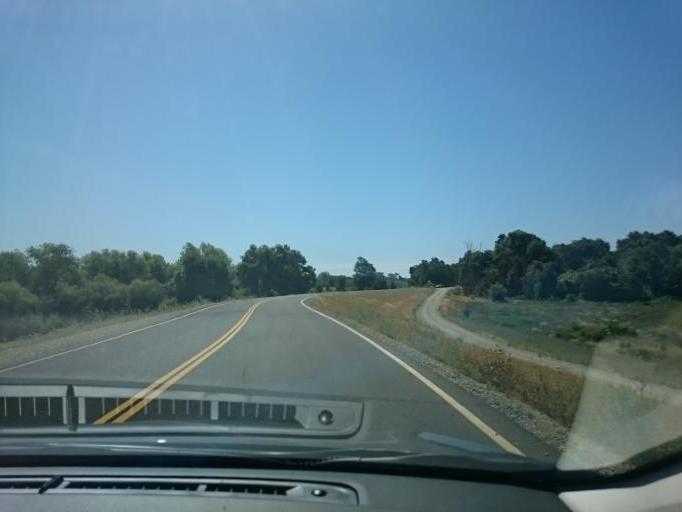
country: US
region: California
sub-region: Yolo County
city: West Sacramento
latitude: 38.5568
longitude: -121.5175
